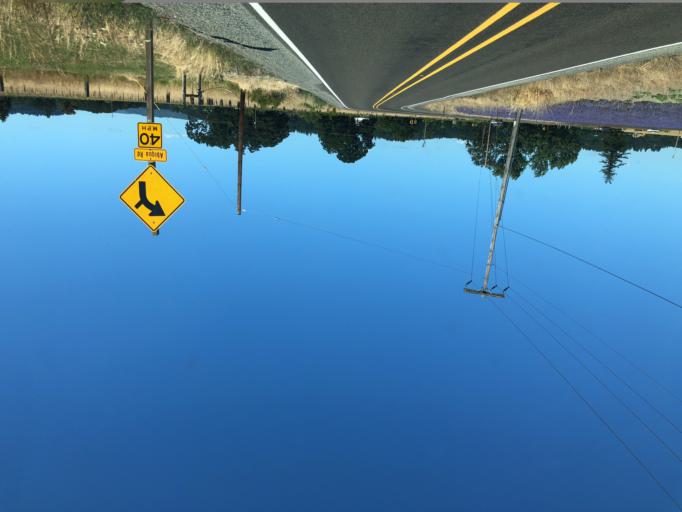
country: US
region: Oregon
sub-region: Marion County
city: Silverton
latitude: 45.0422
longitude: -122.7471
